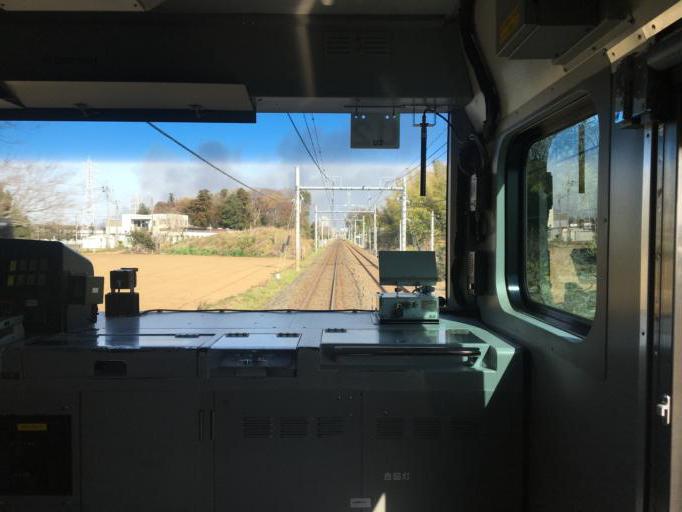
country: JP
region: Ibaraki
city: Koga
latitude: 36.1744
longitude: 139.7155
